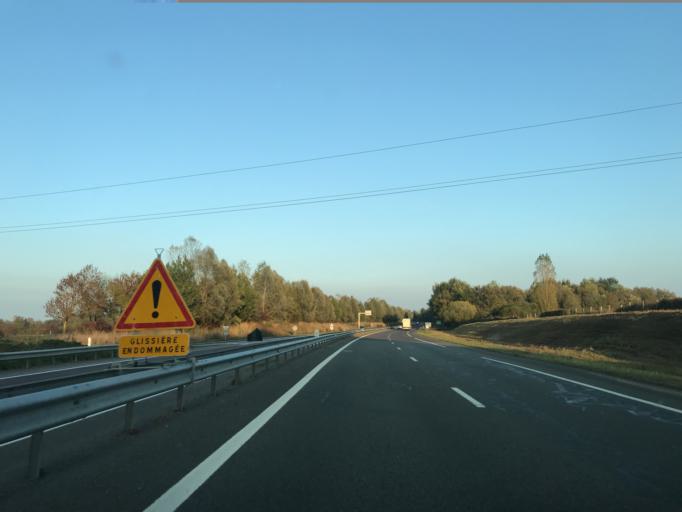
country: FR
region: Pays de la Loire
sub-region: Departement de la Sarthe
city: Mamers
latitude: 48.5060
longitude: 0.3680
